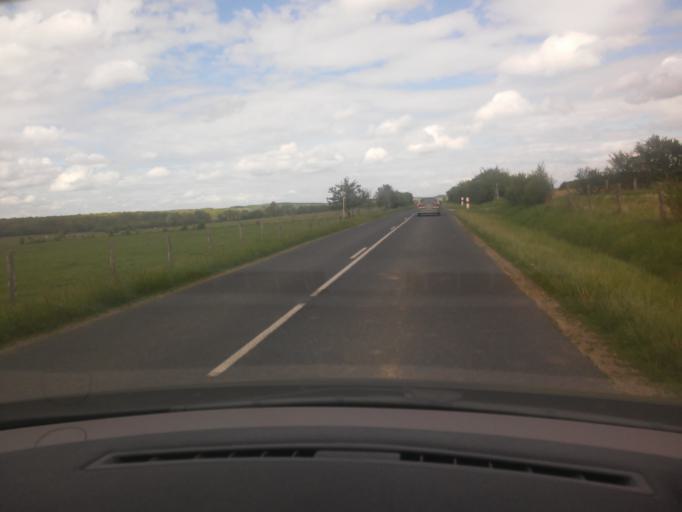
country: FR
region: Lorraine
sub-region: Departement de Meurthe-et-Moselle
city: Longuyon
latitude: 49.3350
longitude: 5.5091
